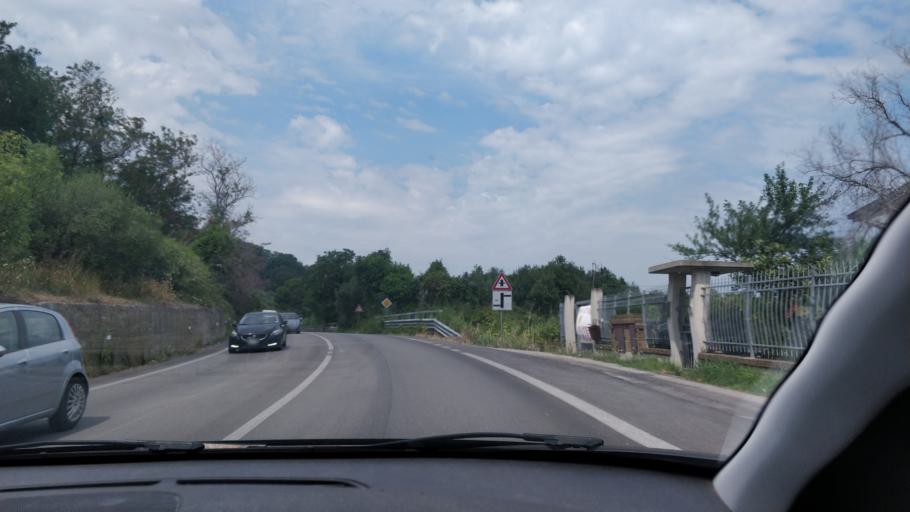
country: IT
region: Abruzzo
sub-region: Provincia di Chieti
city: Marina di San Vito
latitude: 42.3193
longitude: 14.4324
